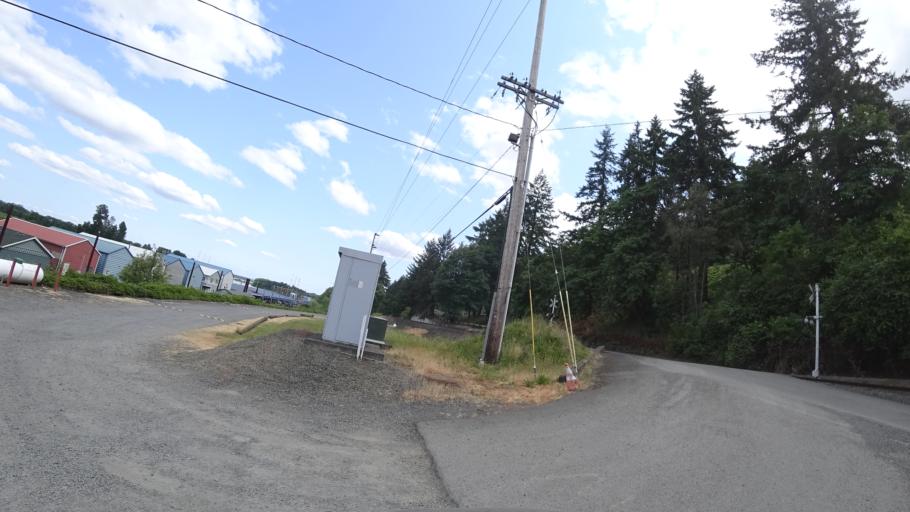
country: US
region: Oregon
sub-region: Washington County
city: Bethany
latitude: 45.6264
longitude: -122.8172
